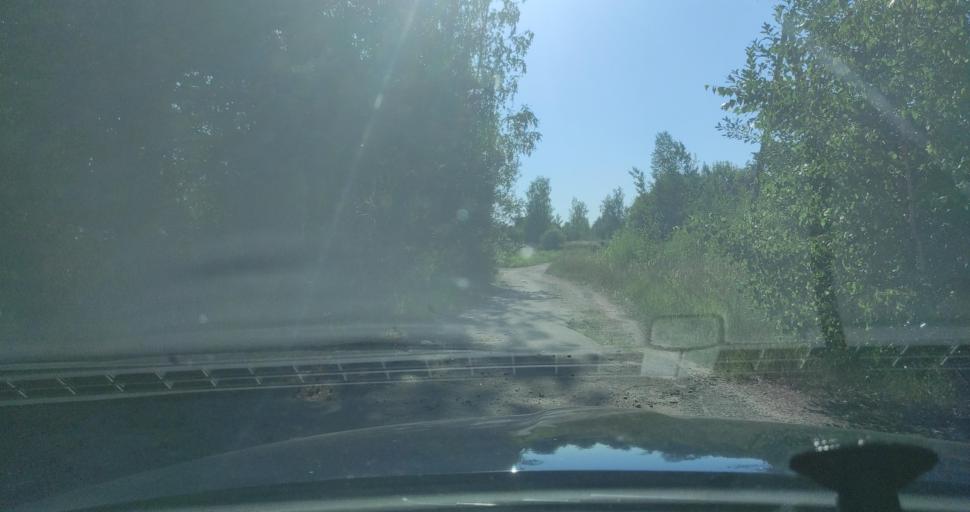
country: LV
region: Skrunda
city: Skrunda
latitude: 56.6814
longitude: 22.0048
